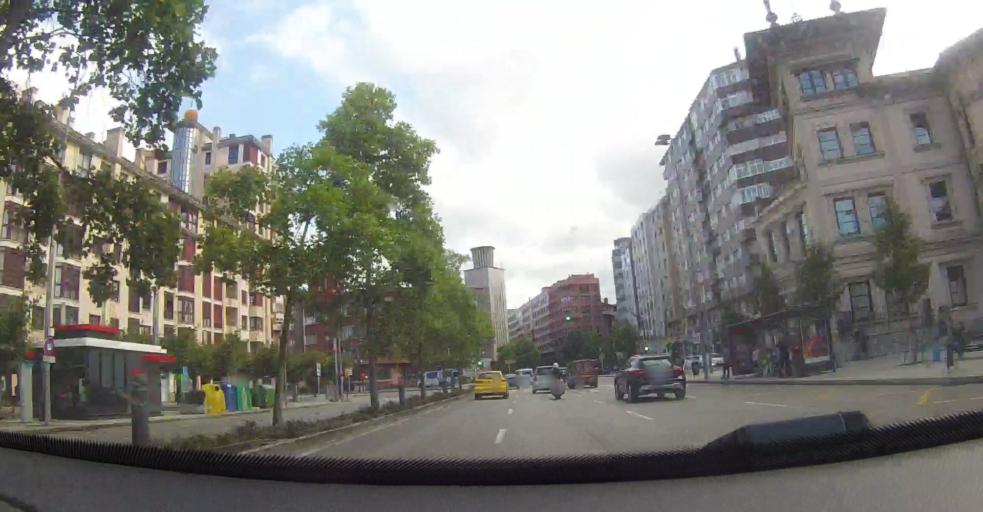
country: ES
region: Asturias
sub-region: Province of Asturias
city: Gijon
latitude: 43.5393
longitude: -5.6662
